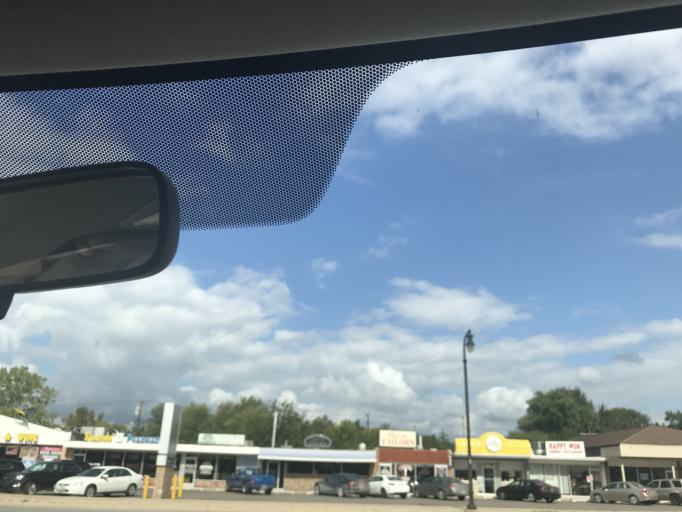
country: US
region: Michigan
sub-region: Washtenaw County
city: Ann Arbor
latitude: 42.2693
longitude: -83.7734
